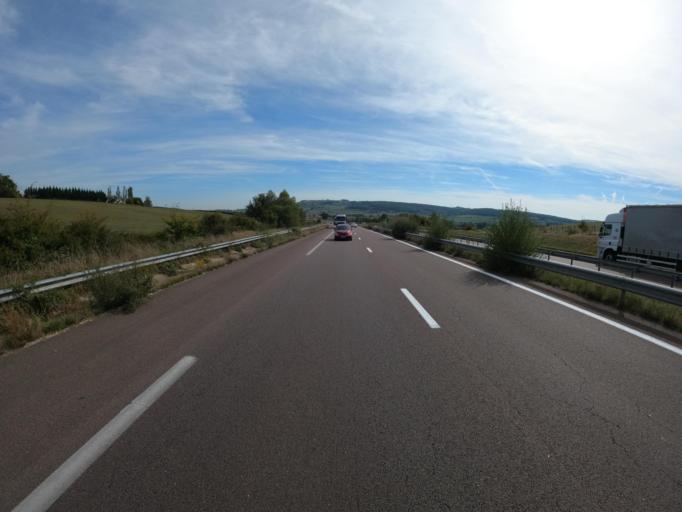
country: FR
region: Bourgogne
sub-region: Departement de Saone-et-Loire
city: Ecuisses
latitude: 46.7370
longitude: 4.6159
